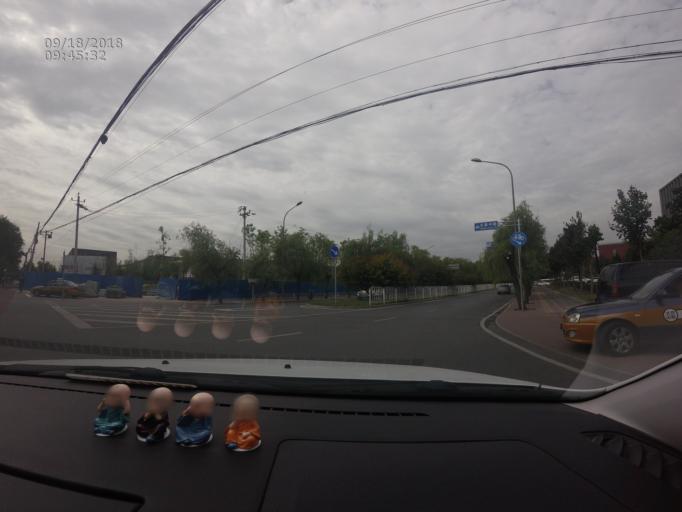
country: CN
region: Beijing
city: Xibeiwang
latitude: 40.0699
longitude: 116.2383
